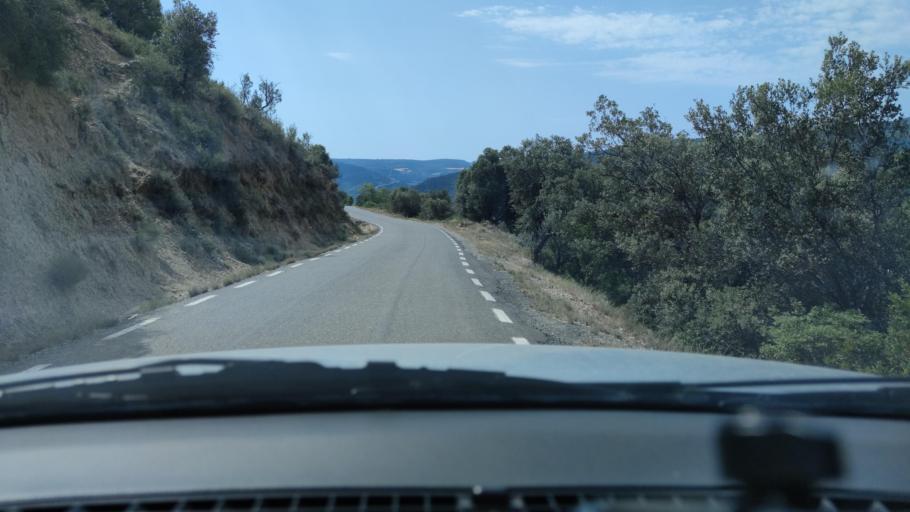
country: ES
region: Catalonia
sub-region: Provincia de Lleida
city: Ager
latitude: 42.0114
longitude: 0.8310
